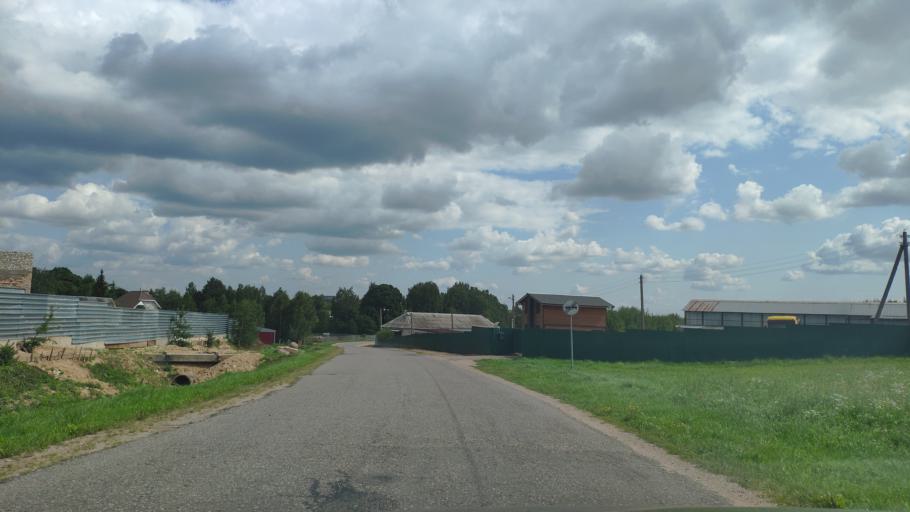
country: BY
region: Minsk
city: Khatsyezhyna
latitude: 53.8546
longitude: 27.3057
